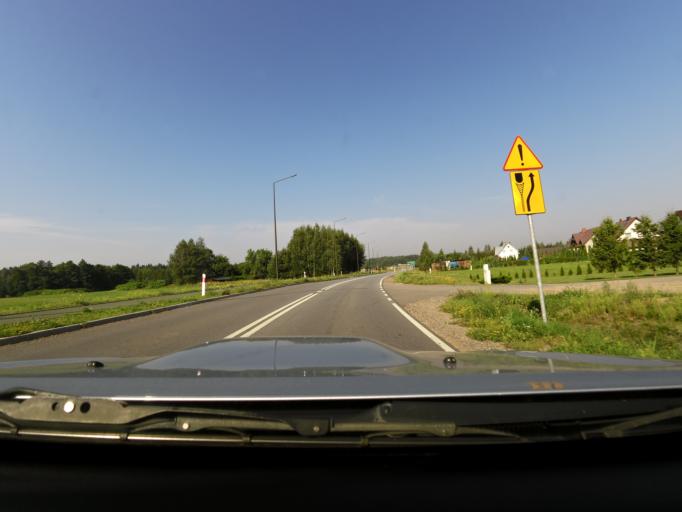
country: PL
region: Podlasie
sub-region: Powiat sejnenski
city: Krasnopol
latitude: 54.0814
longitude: 23.1182
